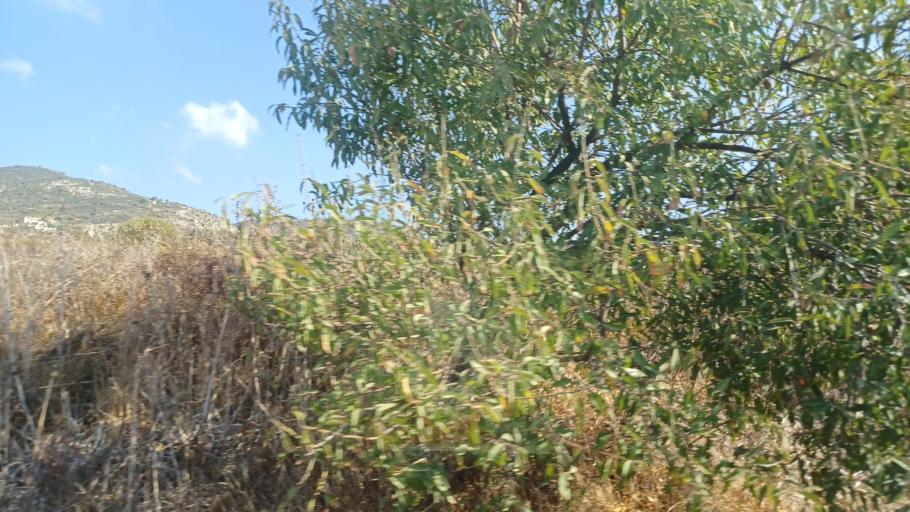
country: CY
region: Pafos
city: Mesogi
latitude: 34.8294
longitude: 32.4515
